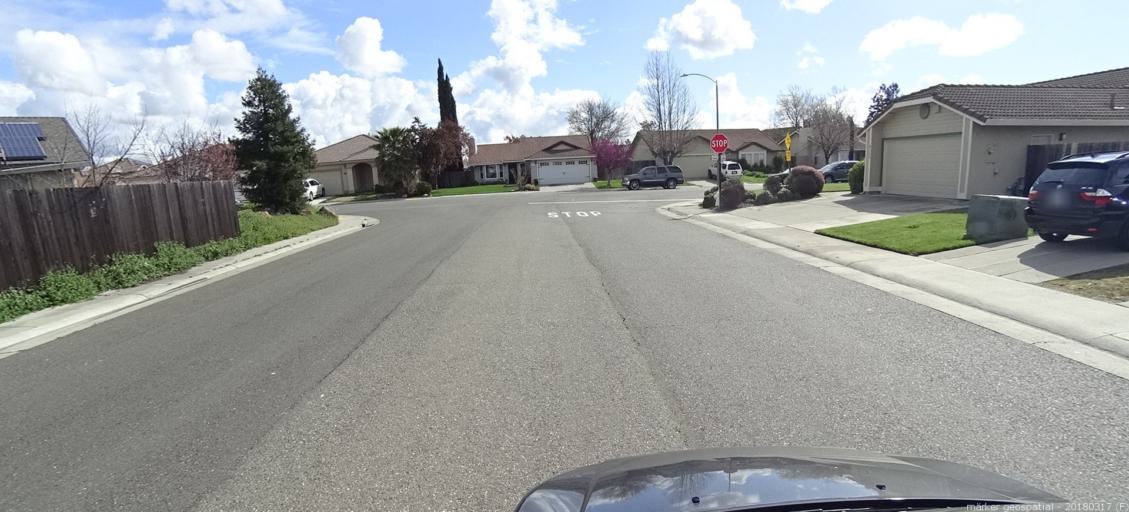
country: US
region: California
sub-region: Sacramento County
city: Florin
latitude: 38.4689
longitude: -121.4056
